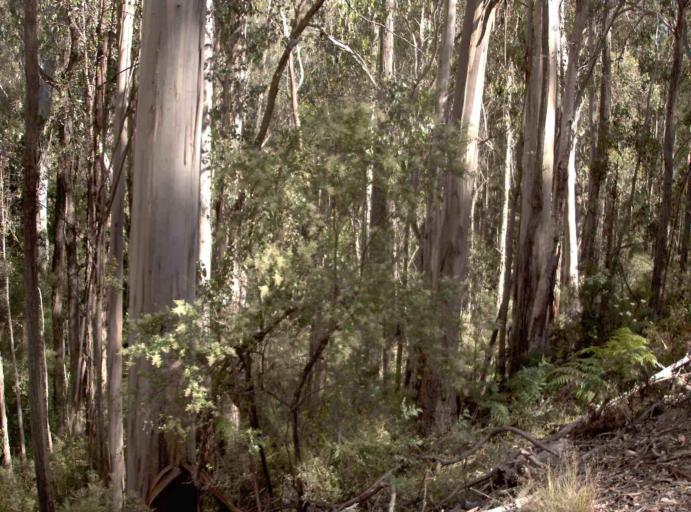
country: AU
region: New South Wales
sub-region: Bombala
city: Bombala
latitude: -37.2897
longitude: 148.7132
